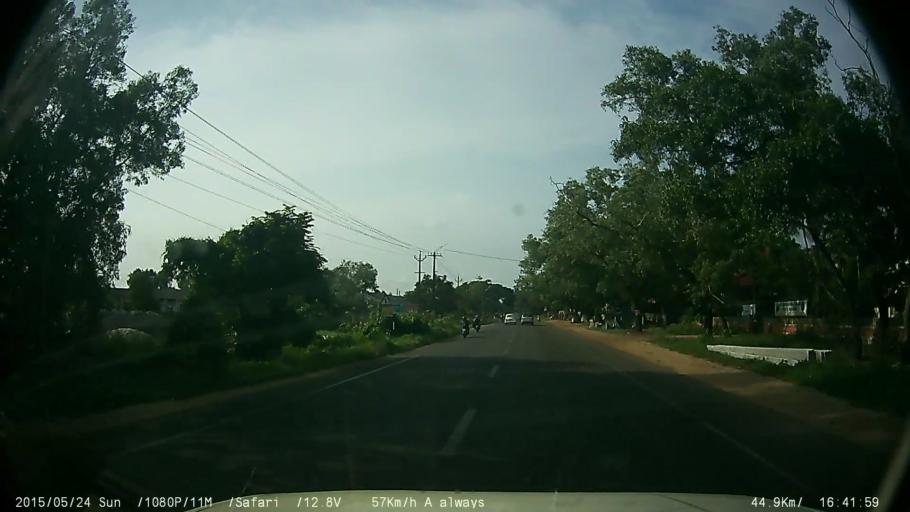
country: IN
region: Kerala
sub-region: Alappuzha
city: Shertallai
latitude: 9.6360
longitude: 76.3344
